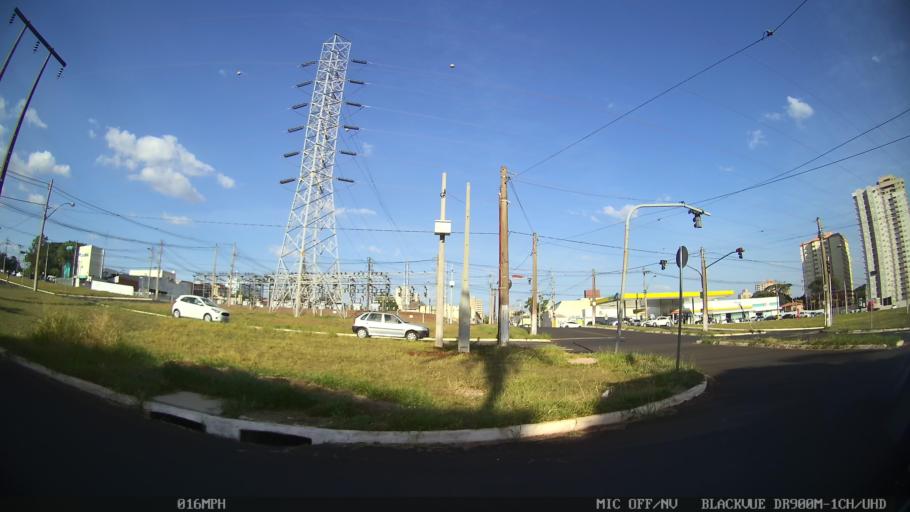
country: BR
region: Sao Paulo
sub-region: Ribeirao Preto
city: Ribeirao Preto
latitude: -21.1949
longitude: -47.7779
